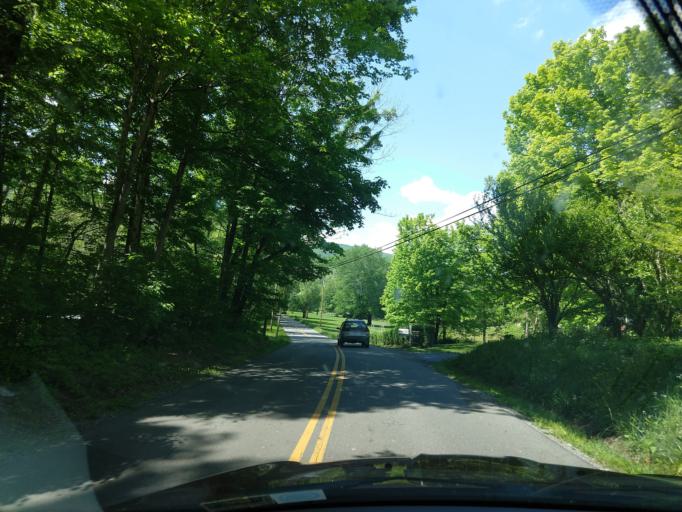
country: US
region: Virginia
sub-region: City of Covington
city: Fairlawn
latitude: 37.6896
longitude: -79.8880
